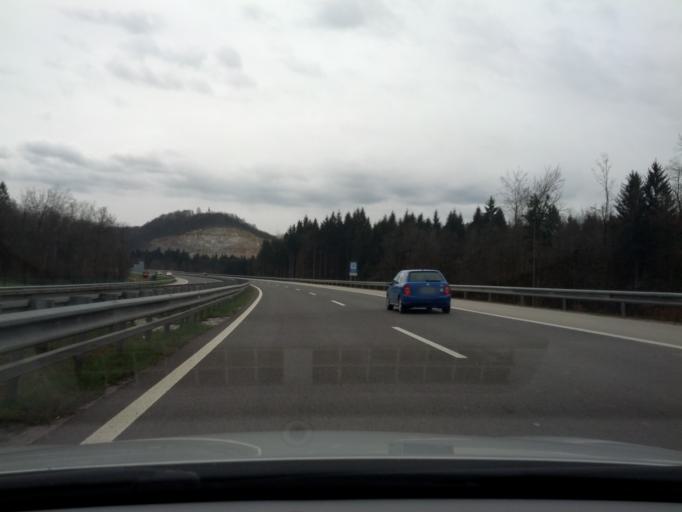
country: SI
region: Trebnje
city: Trebnje
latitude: 45.8939
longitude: 15.0584
